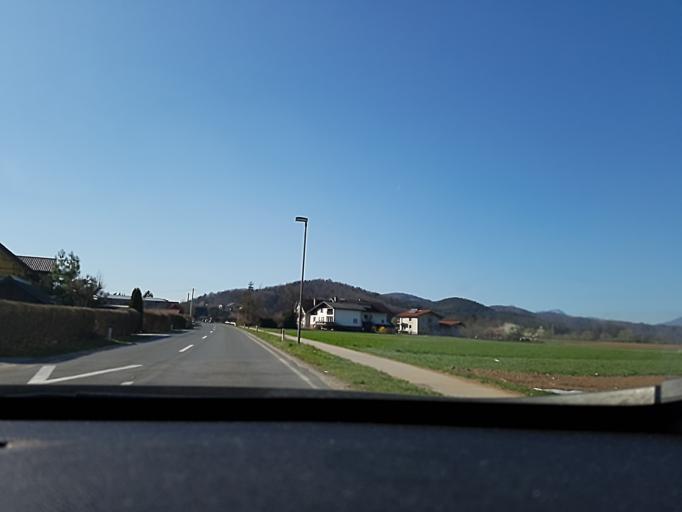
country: SI
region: Trzin
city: Trzin
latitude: 46.1007
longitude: 14.5530
